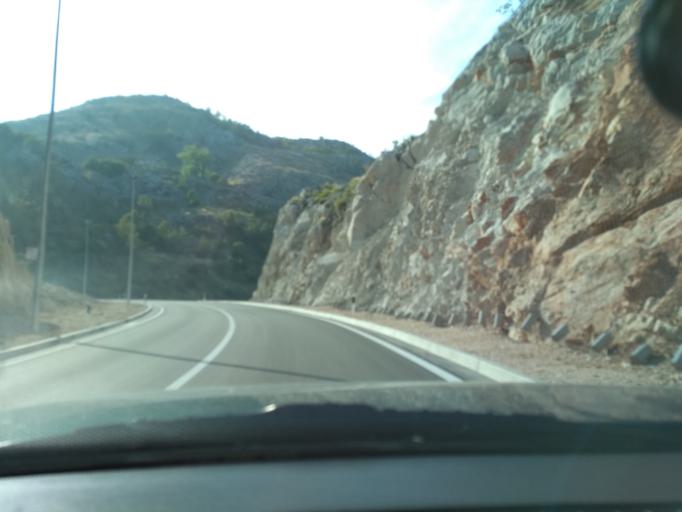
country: ME
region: Cetinje
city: Cetinje
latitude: 42.4377
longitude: 18.8543
